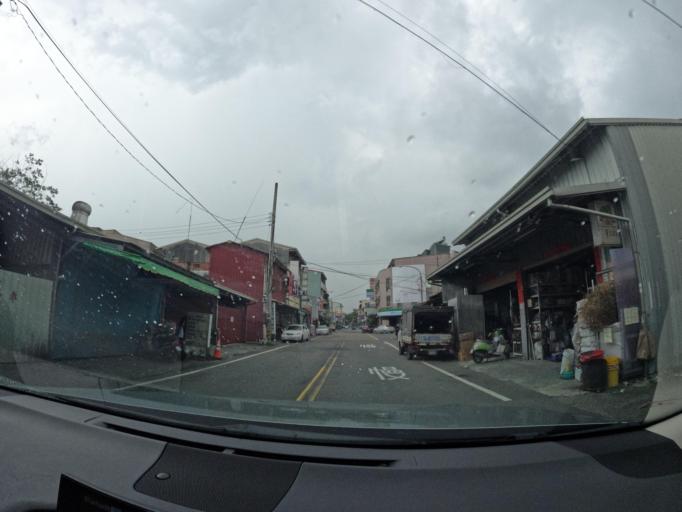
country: TW
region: Taiwan
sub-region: Nantou
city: Nantou
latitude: 23.8795
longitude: 120.7671
